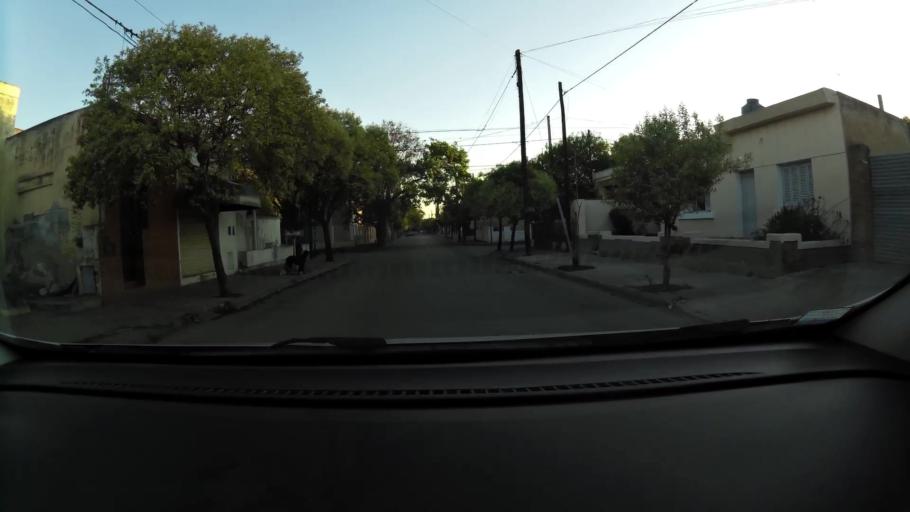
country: AR
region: Cordoba
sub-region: Departamento de Capital
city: Cordoba
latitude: -31.3741
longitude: -64.2165
